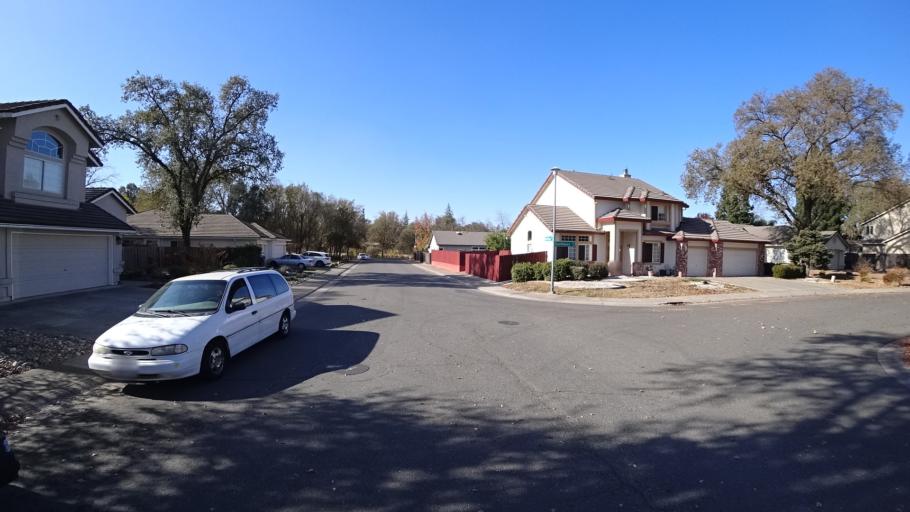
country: US
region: California
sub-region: Sacramento County
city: Citrus Heights
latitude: 38.7017
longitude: -121.2779
